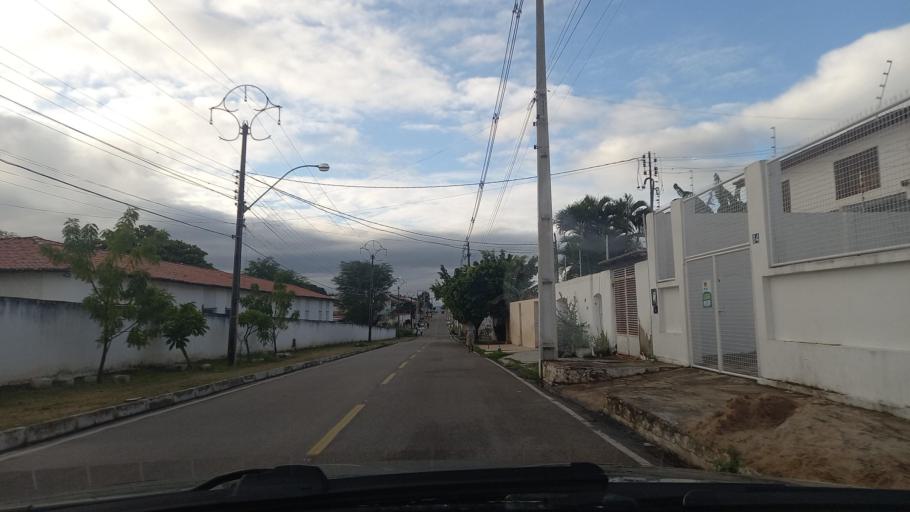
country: BR
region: Bahia
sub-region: Paulo Afonso
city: Paulo Afonso
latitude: -9.3945
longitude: -38.2318
